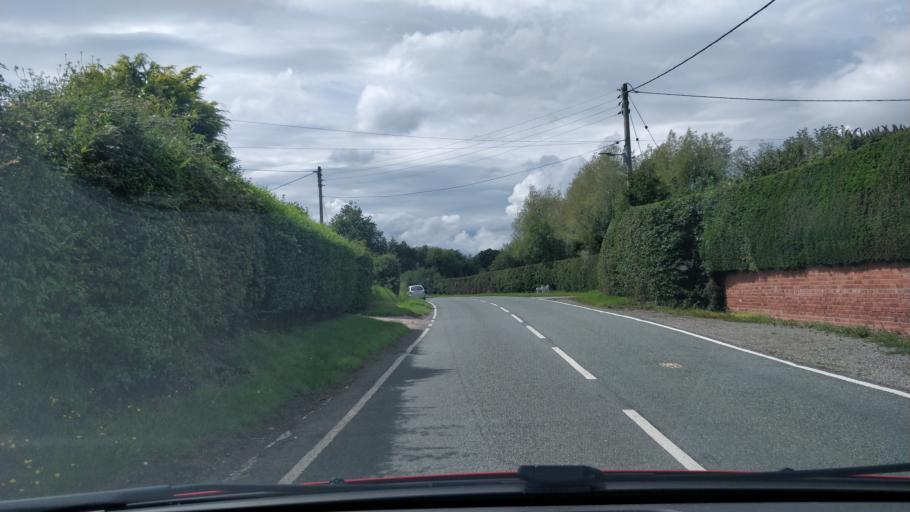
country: GB
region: Wales
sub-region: County of Flintshire
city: Hawarden
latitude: 53.1524
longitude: -2.9843
